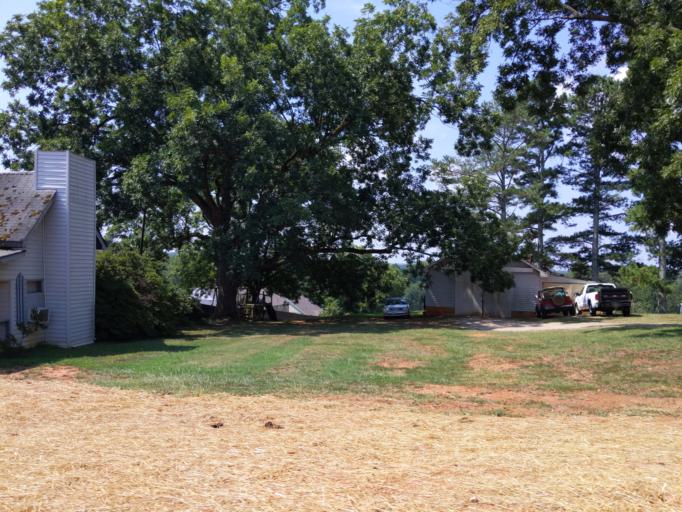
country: US
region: Georgia
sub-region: Hall County
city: Flowery Branch
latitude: 34.1427
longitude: -83.8843
